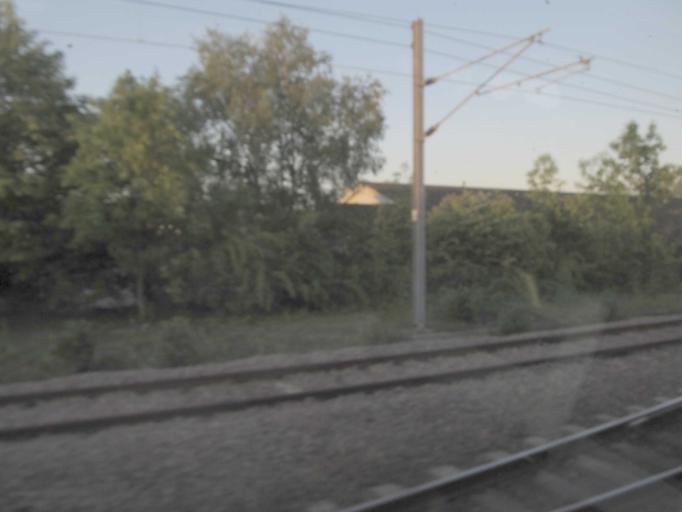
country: GB
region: England
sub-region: Lincolnshire
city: Grantham
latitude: 52.9014
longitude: -0.6360
